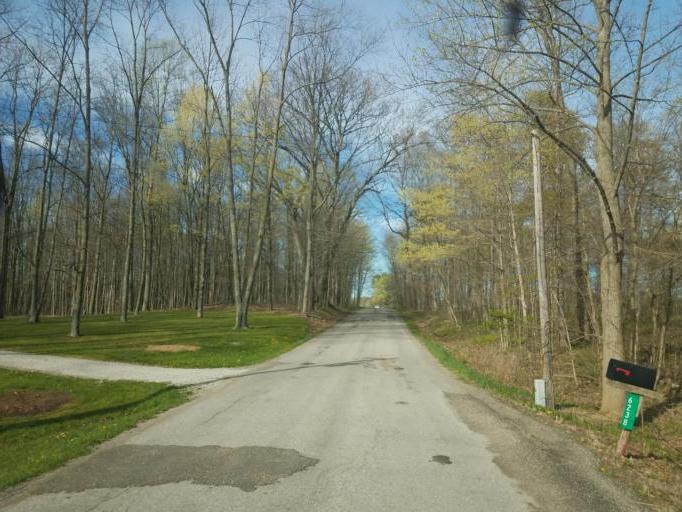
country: US
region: Ohio
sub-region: Morrow County
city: Mount Gilead
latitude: 40.5824
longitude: -82.7880
